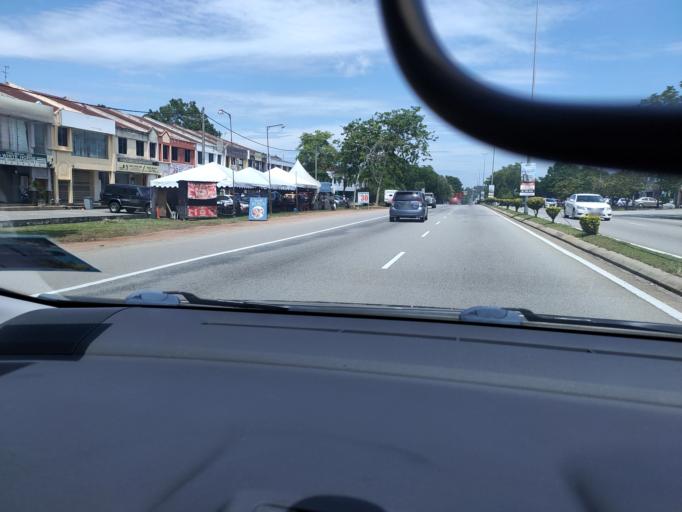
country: MY
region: Melaka
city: Bukit Rambai
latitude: 2.2775
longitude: 102.2152
